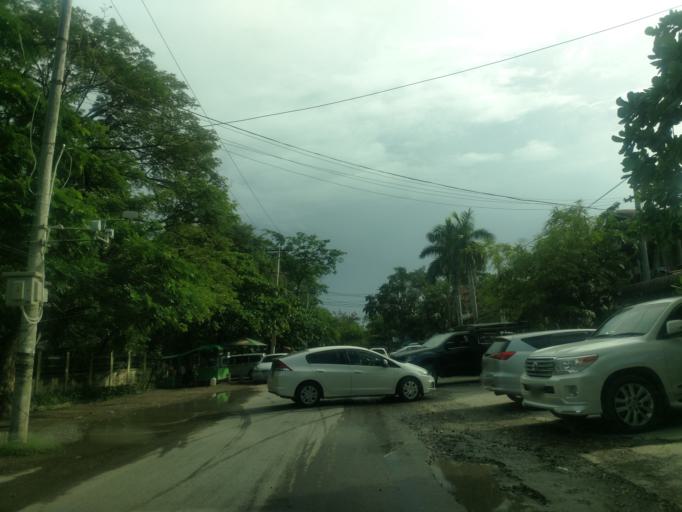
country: MM
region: Mandalay
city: Mandalay
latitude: 21.9783
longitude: 96.1006
